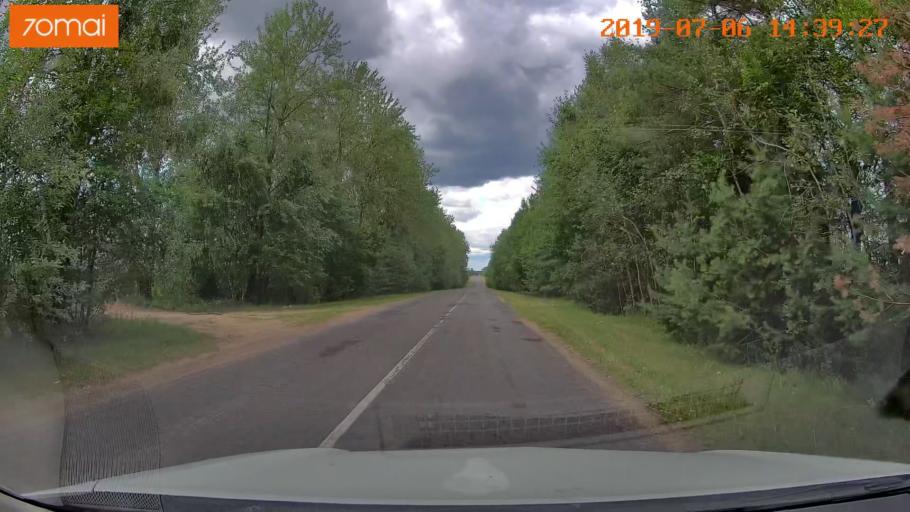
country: BY
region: Minsk
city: Ivyanyets
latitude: 53.9166
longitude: 26.6889
